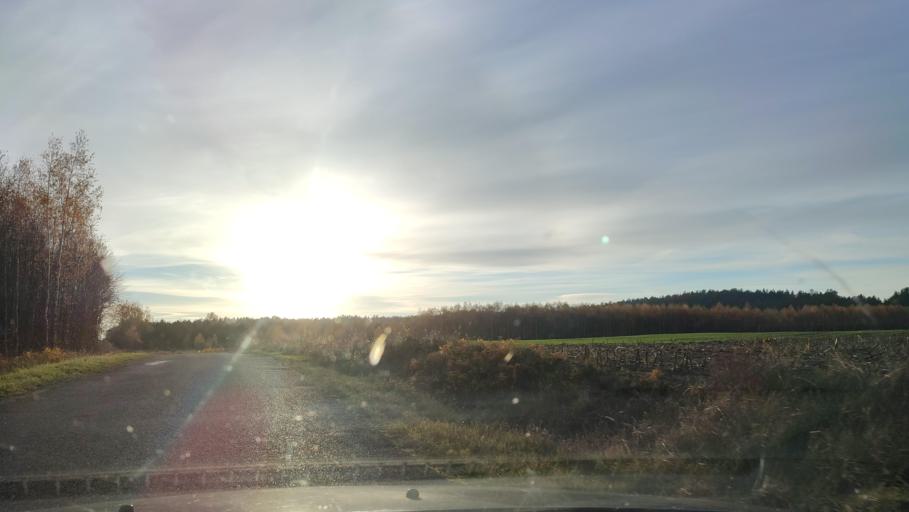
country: PL
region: Masovian Voivodeship
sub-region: Powiat przasnyski
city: Chorzele
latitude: 53.3362
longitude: 20.7476
